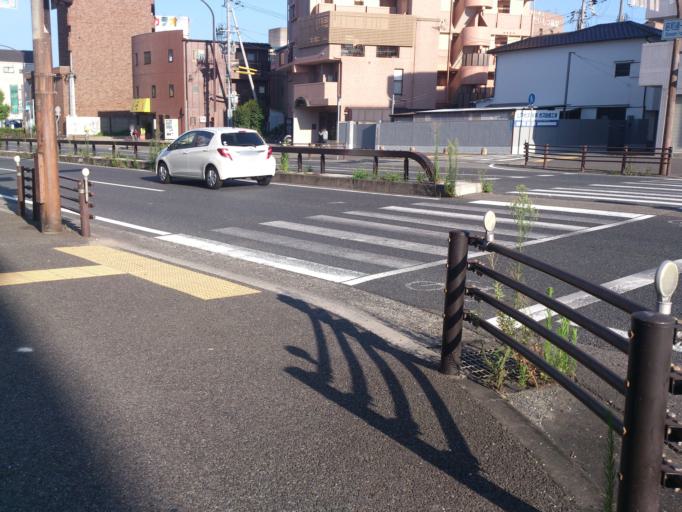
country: JP
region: Hyogo
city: Amagasaki
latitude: 34.7197
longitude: 135.4262
